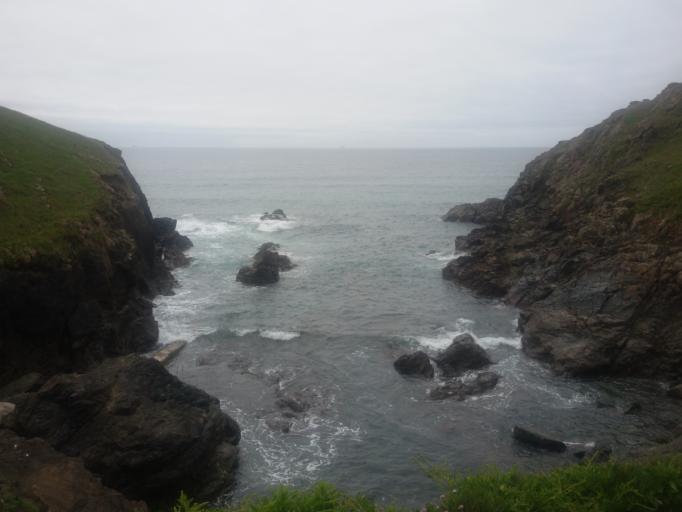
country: GB
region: England
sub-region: Cornwall
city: Landewednack
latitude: 49.9680
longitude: -5.2157
